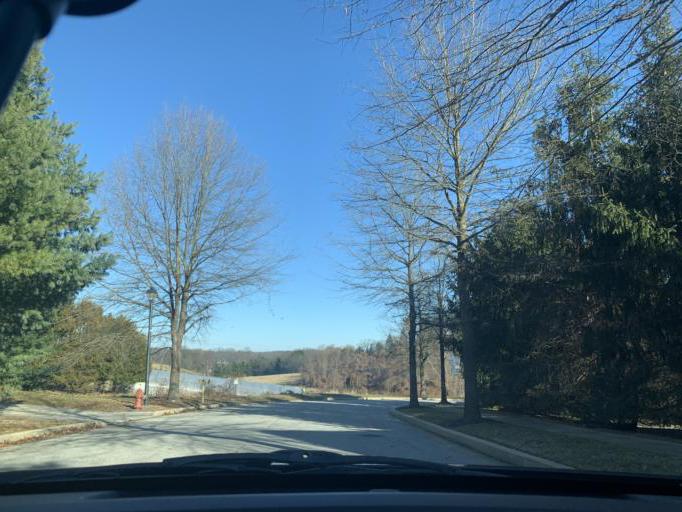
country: US
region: Maryland
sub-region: Baltimore County
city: Garrison
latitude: 39.3972
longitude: -76.7372
